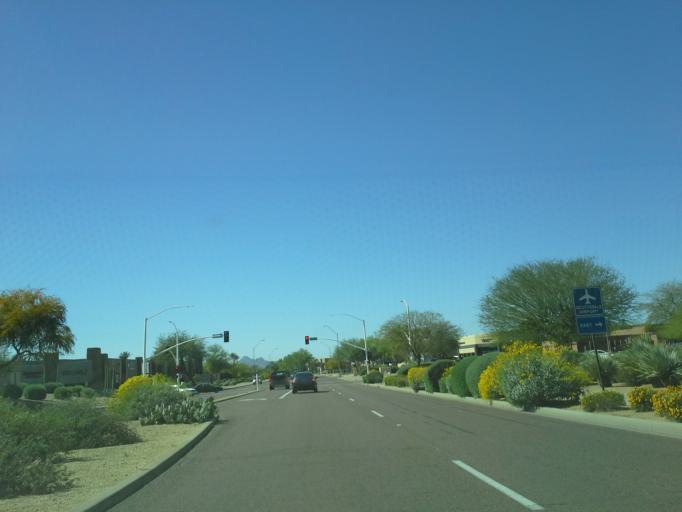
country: US
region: Arizona
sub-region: Maricopa County
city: Paradise Valley
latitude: 33.6242
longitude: -111.9021
